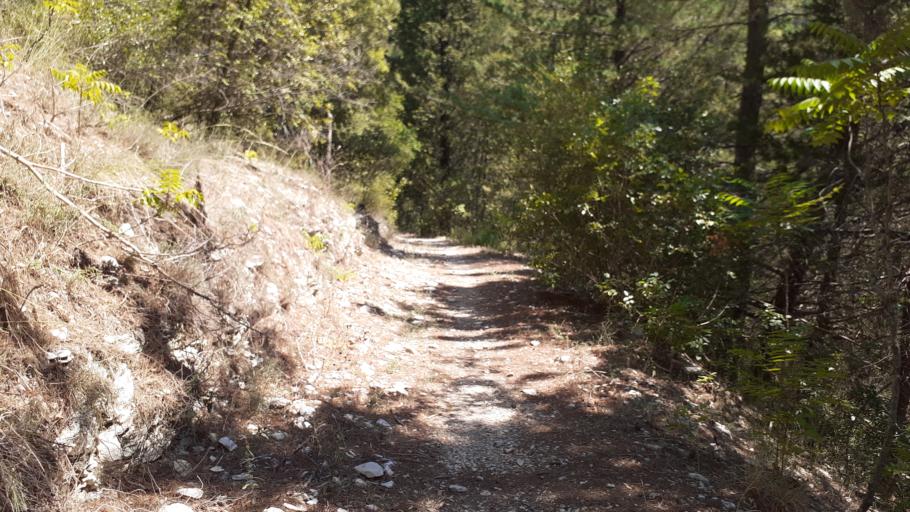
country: IT
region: Abruzzo
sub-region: Provincia di Pescara
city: San Valentino in Abruzzo Citeriore
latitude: 42.2422
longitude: 13.9705
